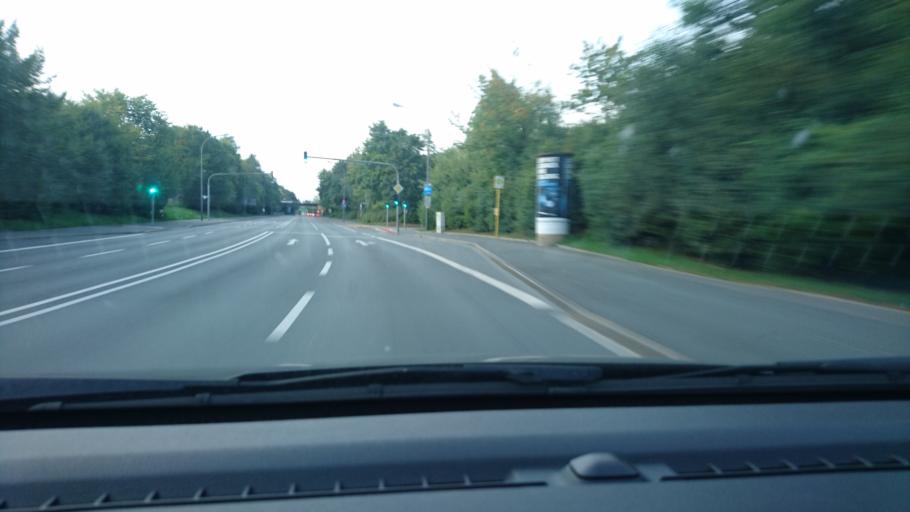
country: DE
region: Bavaria
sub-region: Upper Franconia
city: Bayreuth
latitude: 49.9502
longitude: 11.5987
